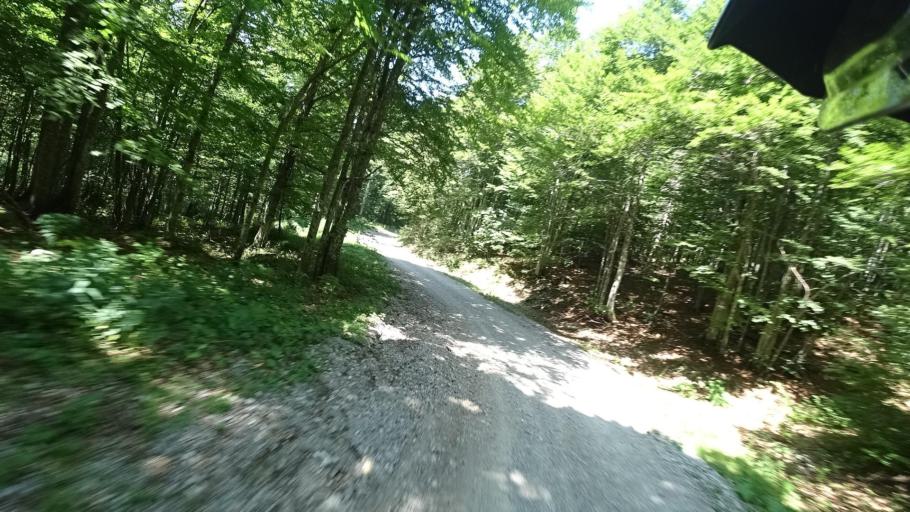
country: HR
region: Primorsko-Goranska
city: Vrbovsko
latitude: 45.2711
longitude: 14.9282
